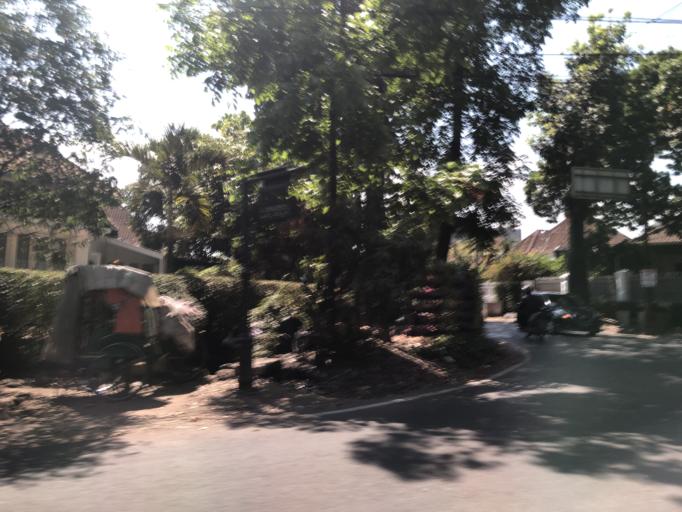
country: ID
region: West Java
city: Bandung
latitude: -6.9111
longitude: 107.6301
